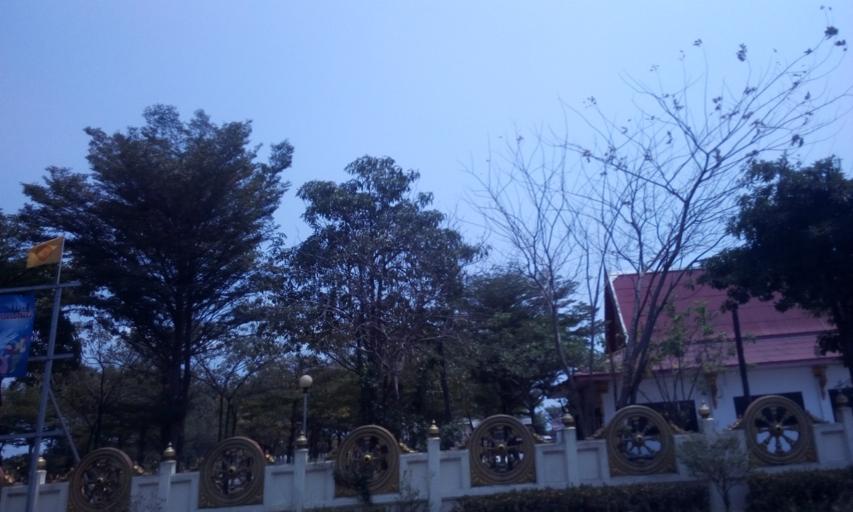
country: TH
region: Chachoengsao
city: Bang Nam Priao
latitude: 13.8629
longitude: 100.9665
